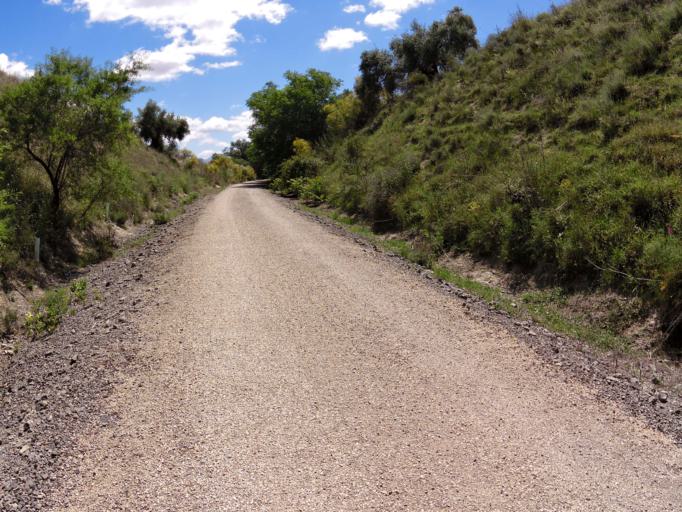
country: ES
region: Andalusia
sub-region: Provincia de Jaen
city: Alcaudete
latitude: 37.6650
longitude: -4.0530
